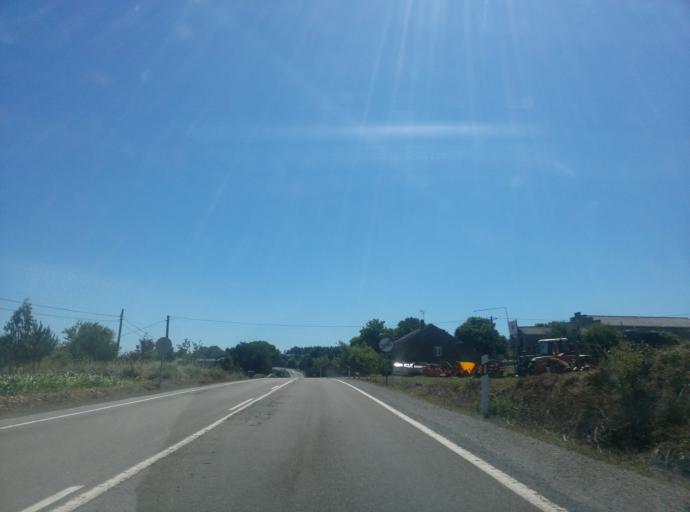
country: ES
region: Galicia
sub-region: Provincia de Lugo
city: Meira
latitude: 43.2051
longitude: -7.3298
